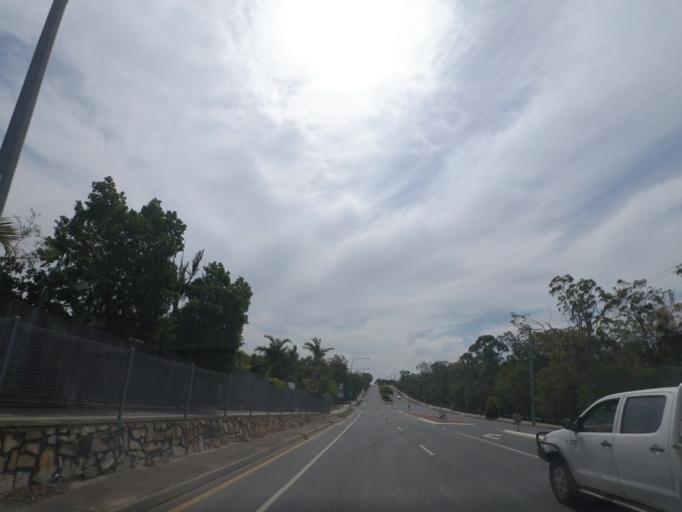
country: AU
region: Queensland
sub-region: Brisbane
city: Sunnybank Hills
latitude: -27.6398
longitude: 153.0541
